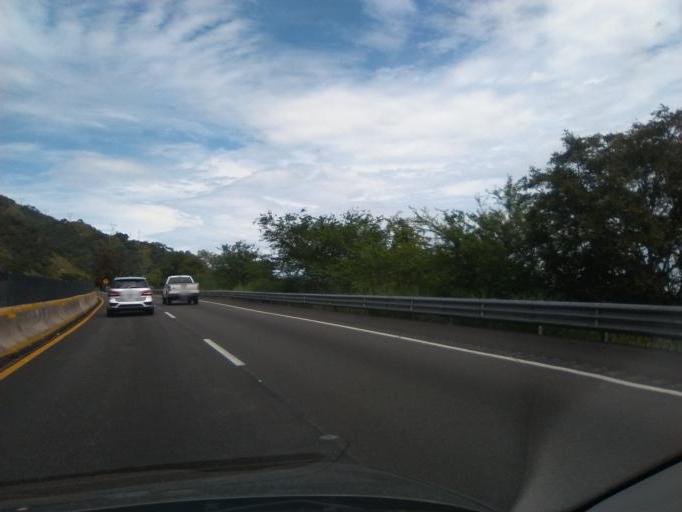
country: MX
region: Guerrero
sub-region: Chilpancingo de los Bravo
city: Cajelitos
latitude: 17.3048
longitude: -99.4962
